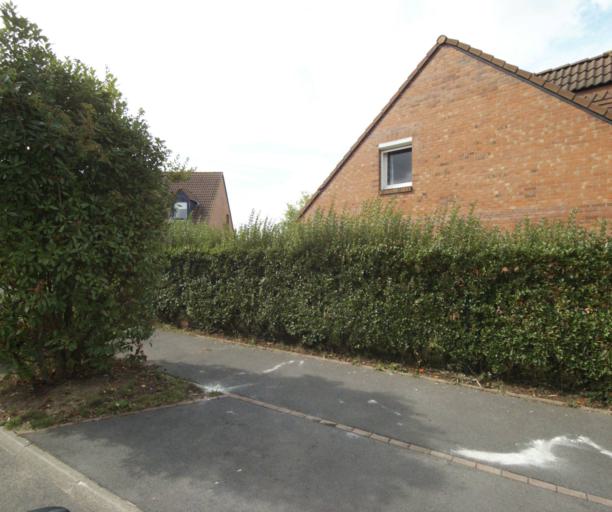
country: FR
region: Nord-Pas-de-Calais
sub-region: Departement du Nord
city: Faches-Thumesnil
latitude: 50.6002
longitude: 3.0598
